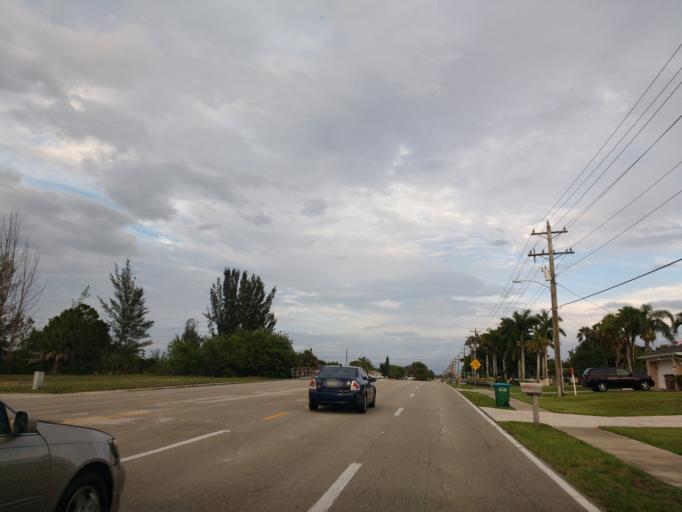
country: US
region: Florida
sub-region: Lee County
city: Cape Coral
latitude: 26.6229
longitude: -81.9852
